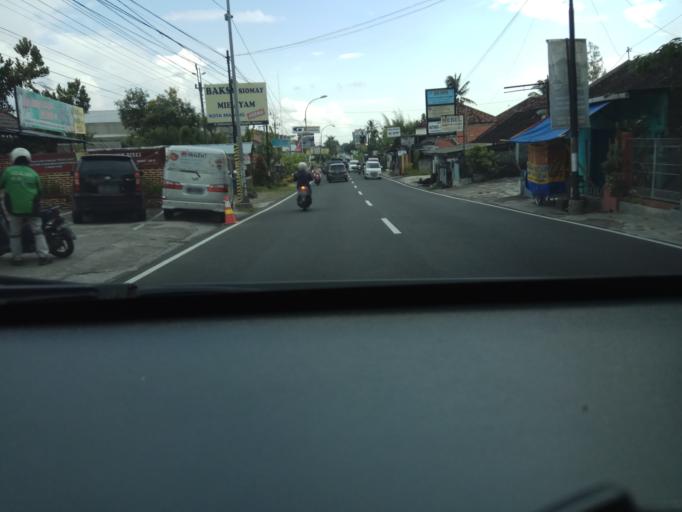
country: ID
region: Daerah Istimewa Yogyakarta
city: Melati
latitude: -7.7066
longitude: 110.4115
